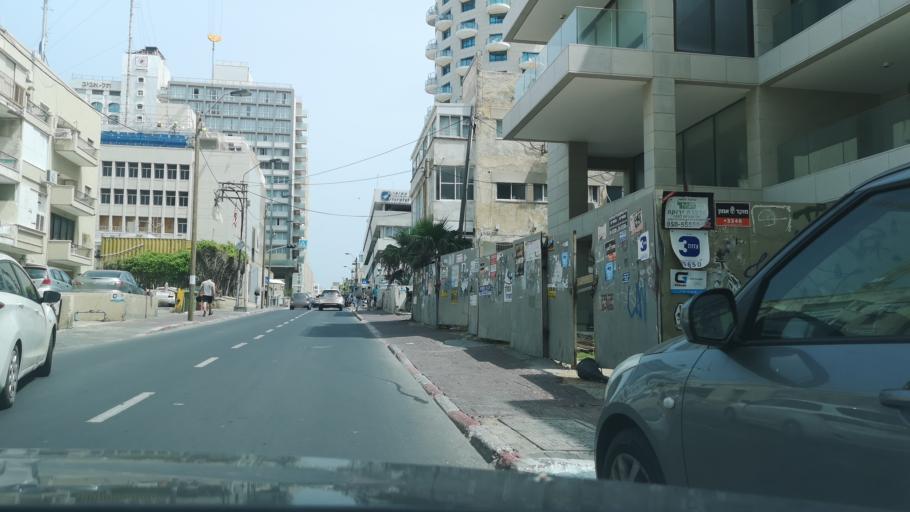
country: IL
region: Tel Aviv
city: Tel Aviv
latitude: 32.0757
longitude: 34.7667
